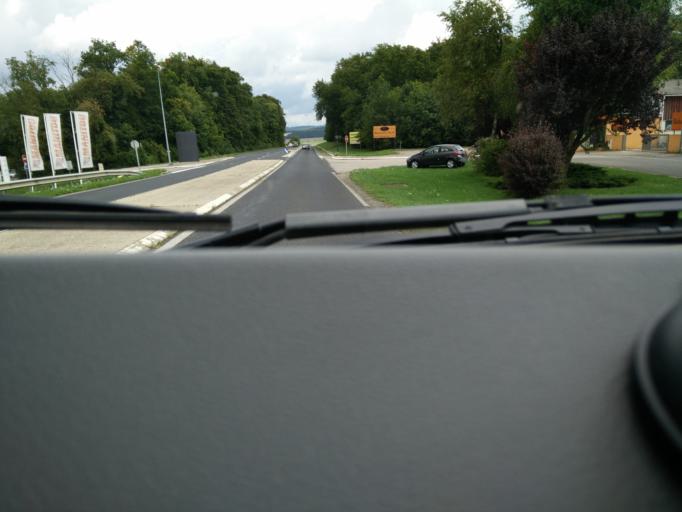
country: FR
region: Lorraine
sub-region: Departement de la Meuse
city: Belleville-sur-Meuse
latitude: 49.1855
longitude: 5.3716
